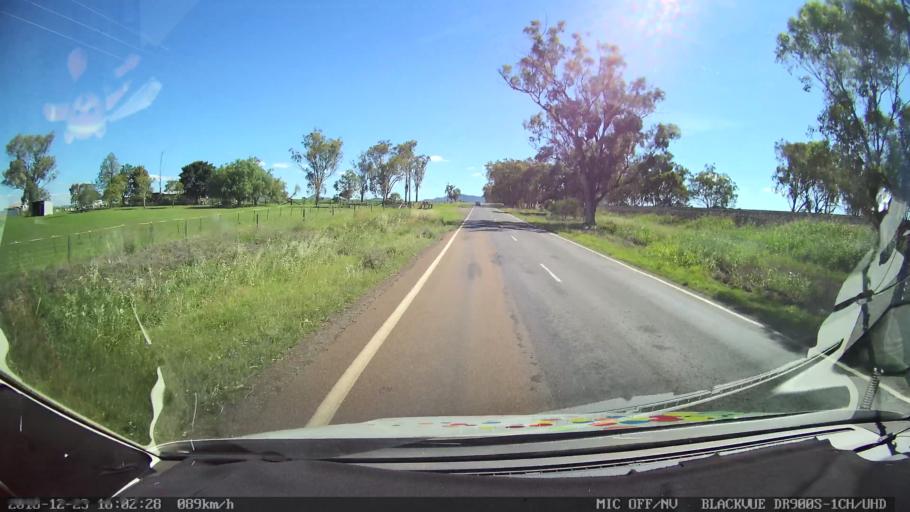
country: AU
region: New South Wales
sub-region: Tamworth Municipality
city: Phillip
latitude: -31.2326
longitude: 150.8087
